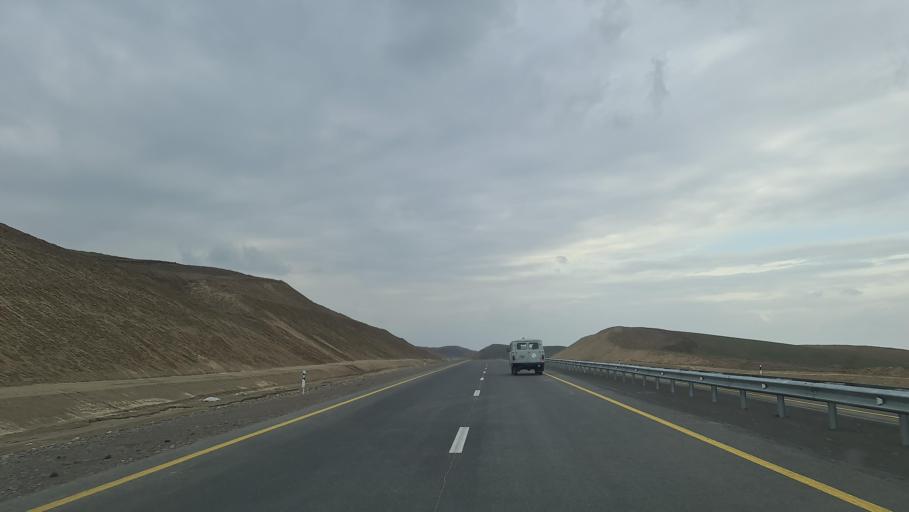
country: KZ
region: Almaty Oblysy
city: Burunday
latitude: 43.2963
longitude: 76.2141
